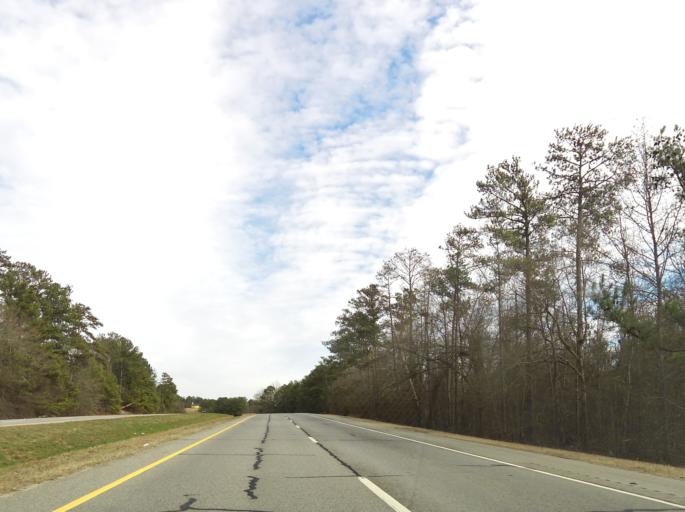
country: US
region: Georgia
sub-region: Bibb County
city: West Point
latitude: 32.8004
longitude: -83.7454
